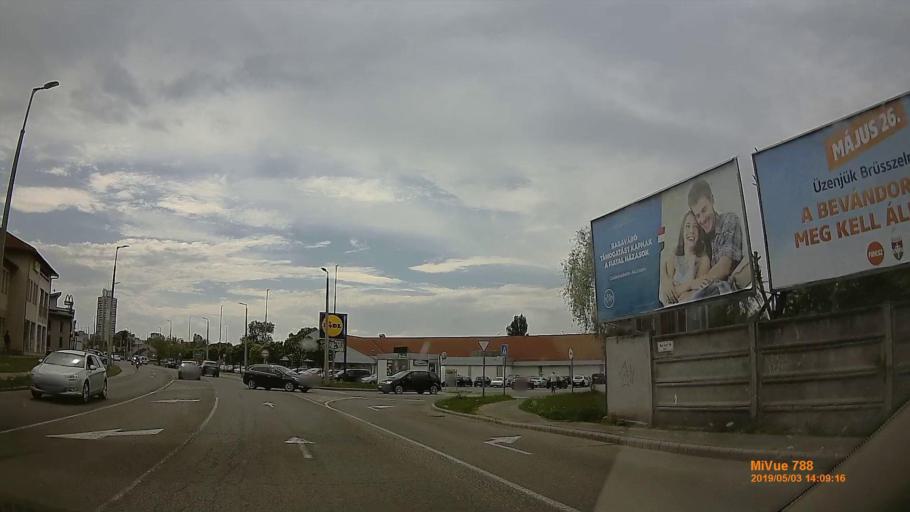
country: HU
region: Jasz-Nagykun-Szolnok
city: Szolnok
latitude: 47.1837
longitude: 20.1853
